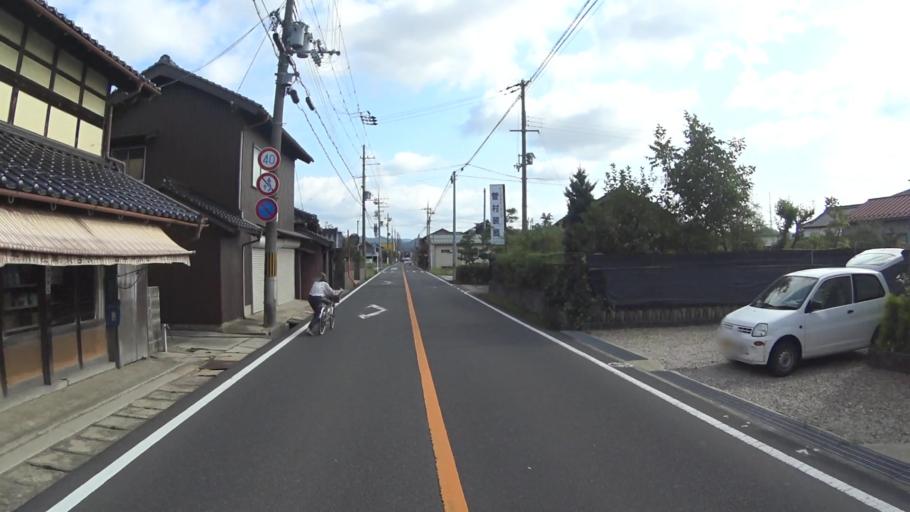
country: JP
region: Kyoto
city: Miyazu
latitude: 35.6077
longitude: 135.0871
